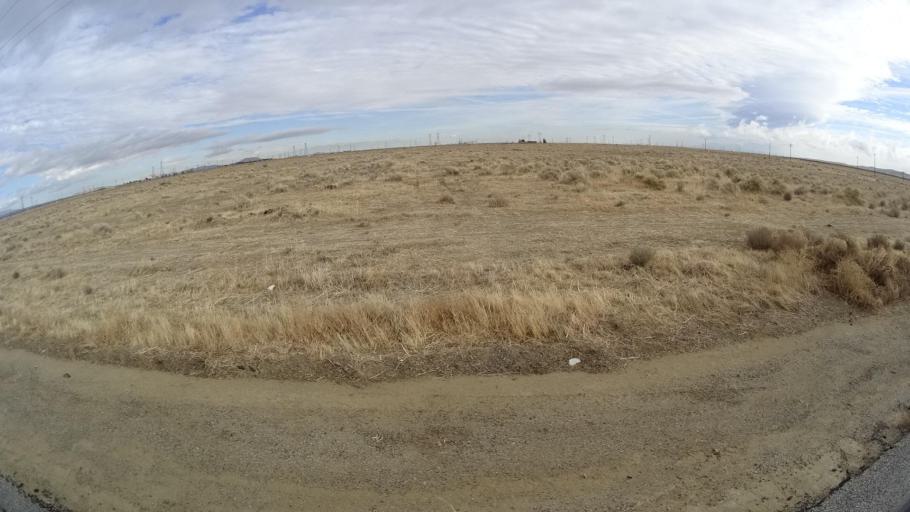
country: US
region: California
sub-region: Los Angeles County
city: Green Valley
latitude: 34.8203
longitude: -118.4316
